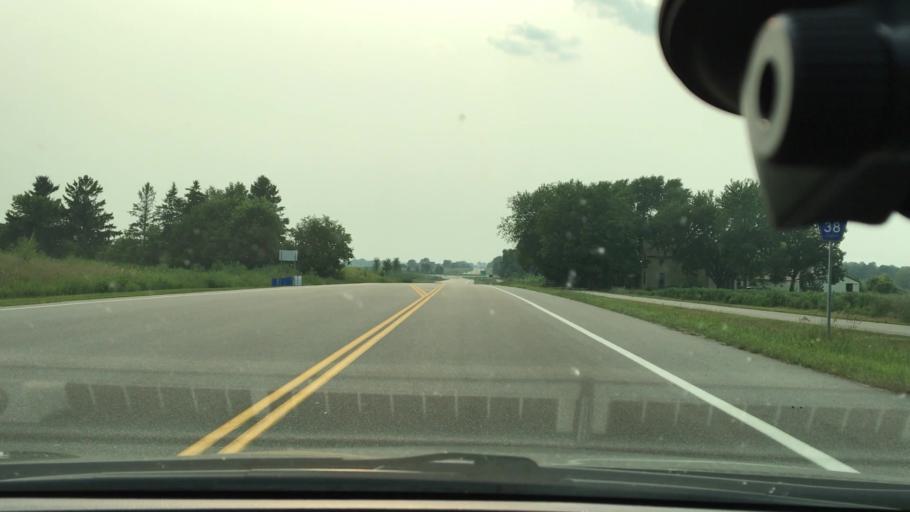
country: US
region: Minnesota
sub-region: Wright County
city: Otsego
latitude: 45.2525
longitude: -93.5921
